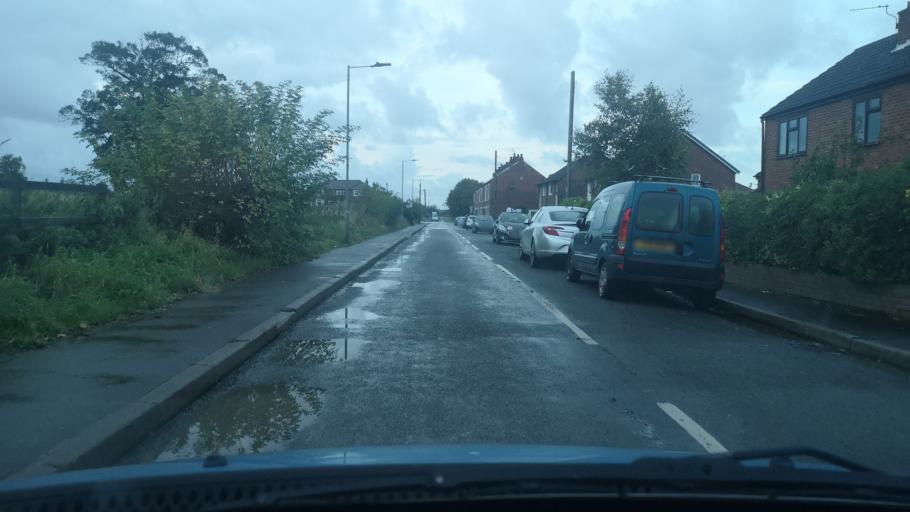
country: GB
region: England
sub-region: Doncaster
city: Norton
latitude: 53.6303
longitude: -1.1846
